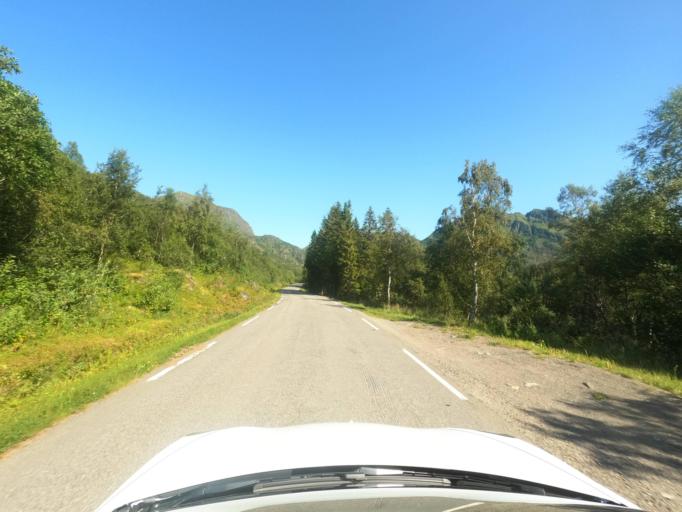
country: NO
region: Nordland
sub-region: Hadsel
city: Stokmarknes
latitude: 68.3047
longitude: 15.0510
